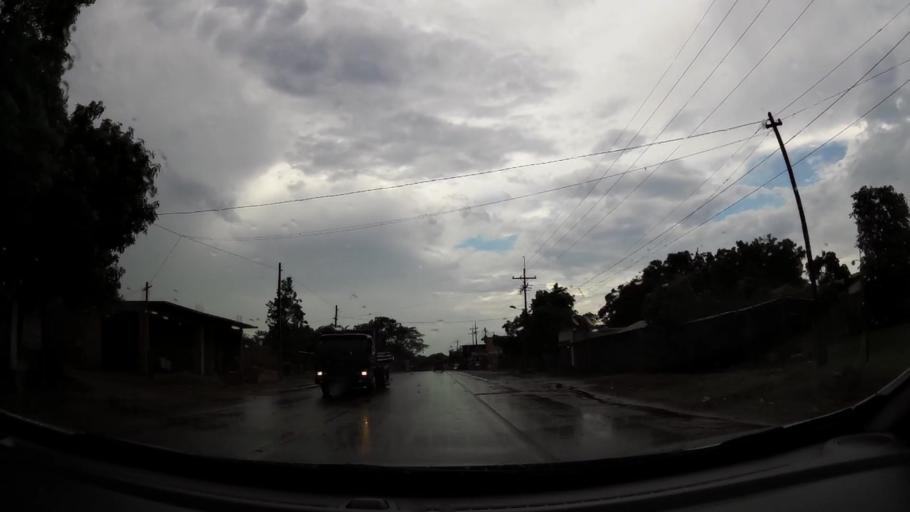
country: PY
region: Alto Parana
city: Presidente Franco
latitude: -25.5681
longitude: -54.6700
